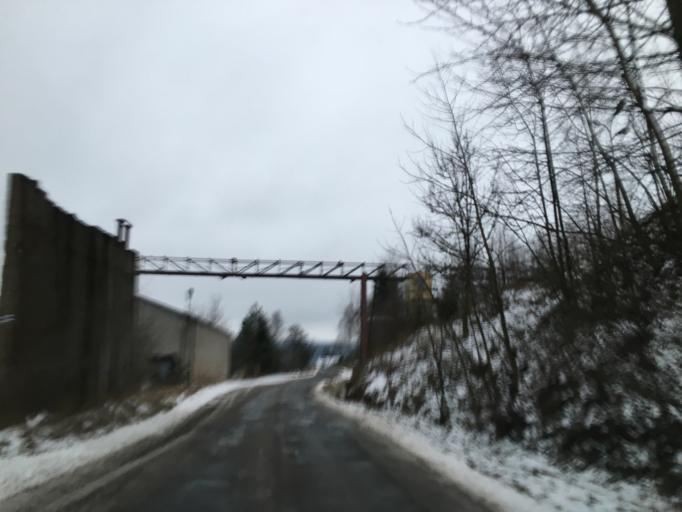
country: CZ
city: Radvanice
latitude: 50.6237
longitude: 16.0316
